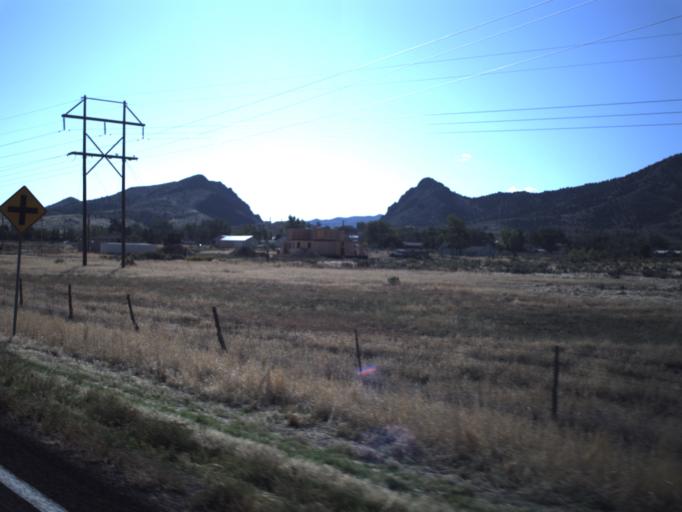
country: US
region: Utah
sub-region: Washington County
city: Enterprise
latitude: 37.6725
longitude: -113.5526
